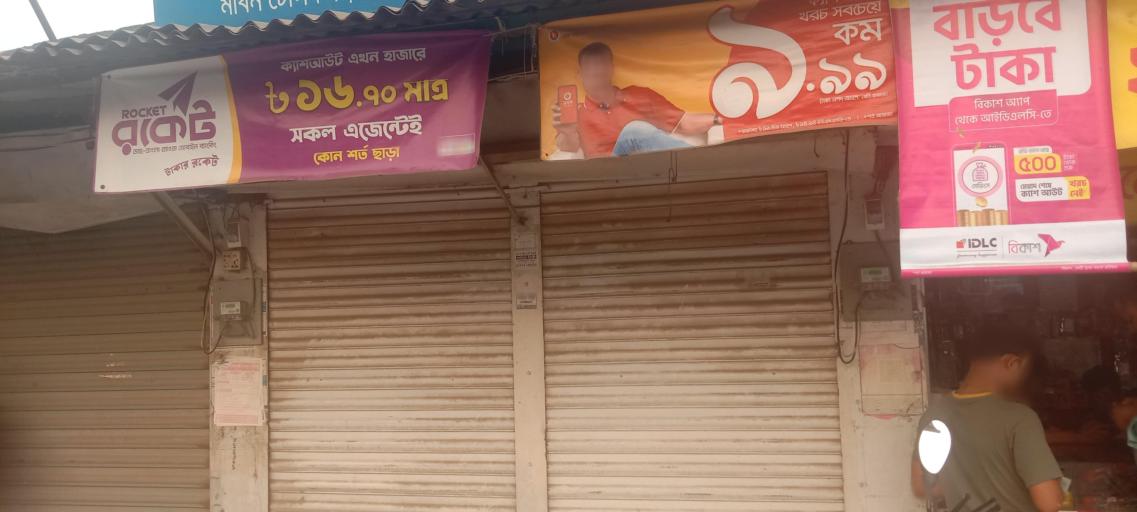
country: BD
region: Dhaka
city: Gafargaon
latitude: 24.2951
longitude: 90.3894
